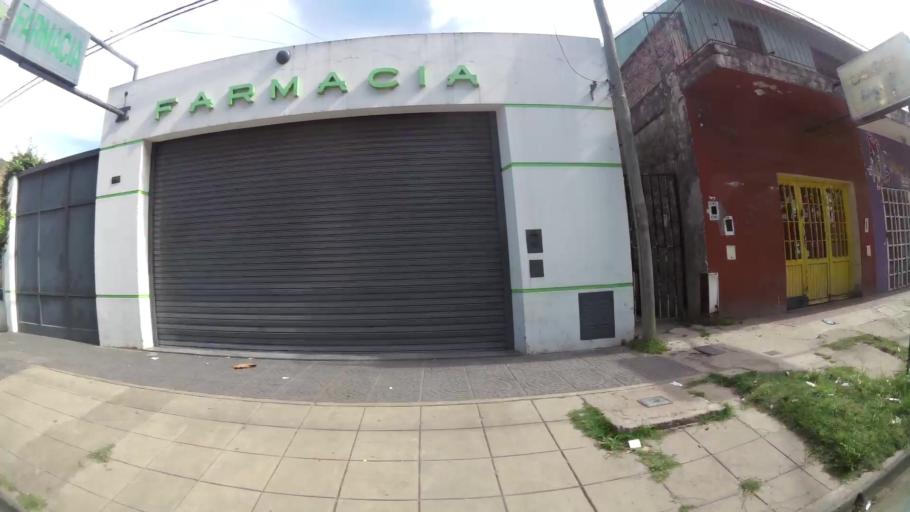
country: AR
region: Santa Fe
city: Granadero Baigorria
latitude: -32.9151
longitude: -60.7202
